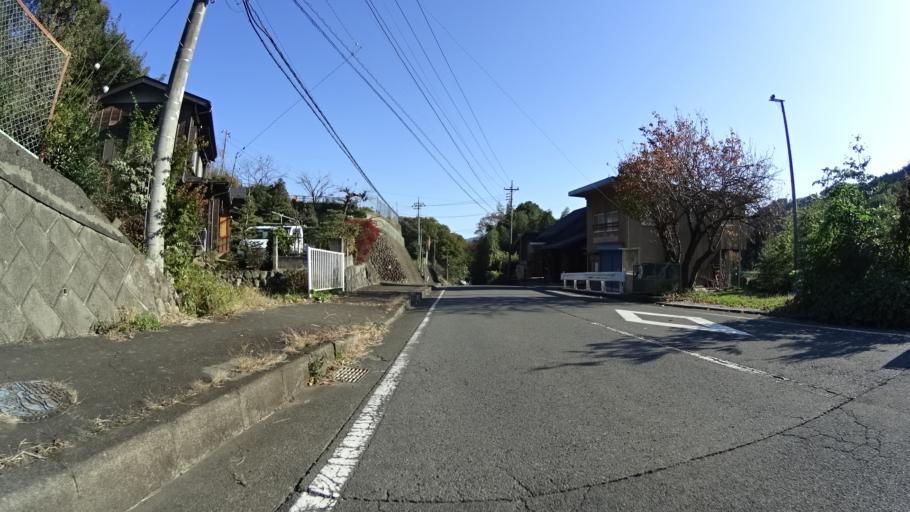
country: JP
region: Yamanashi
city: Uenohara
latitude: 35.6481
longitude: 139.1228
